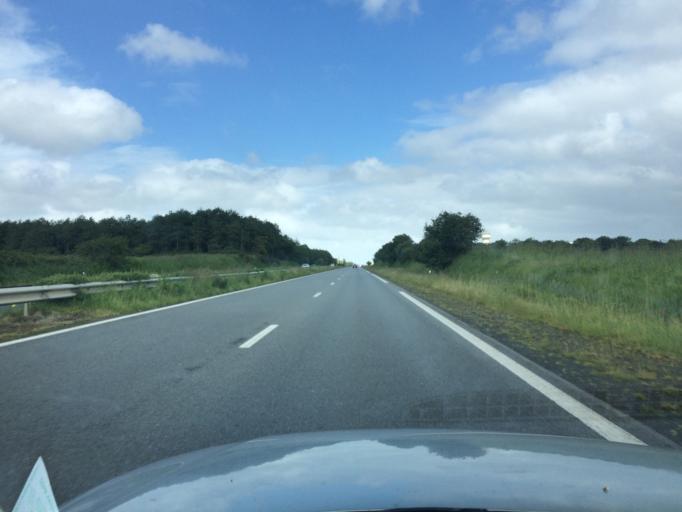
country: FR
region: Brittany
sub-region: Departement du Finistere
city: Saint-Thonan
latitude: 48.4653
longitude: -4.3443
